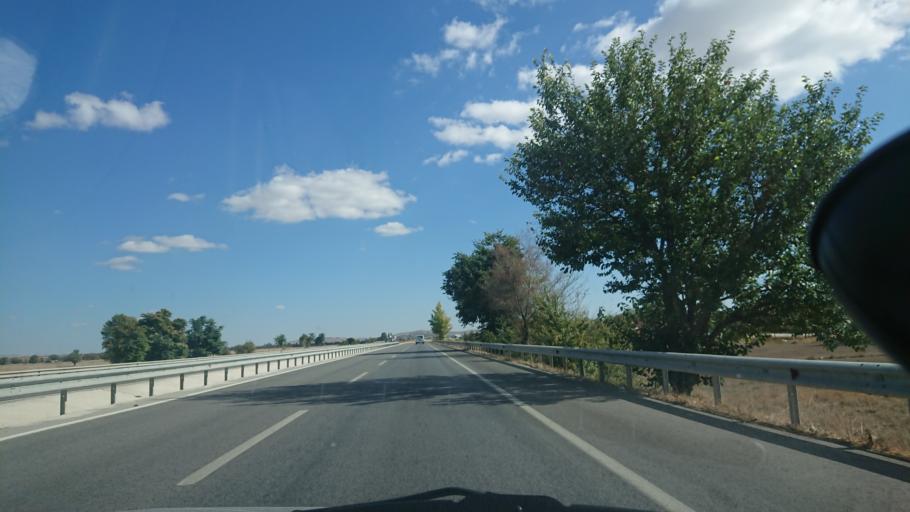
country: TR
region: Eskisehir
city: Mahmudiye
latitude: 39.5414
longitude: 30.9383
